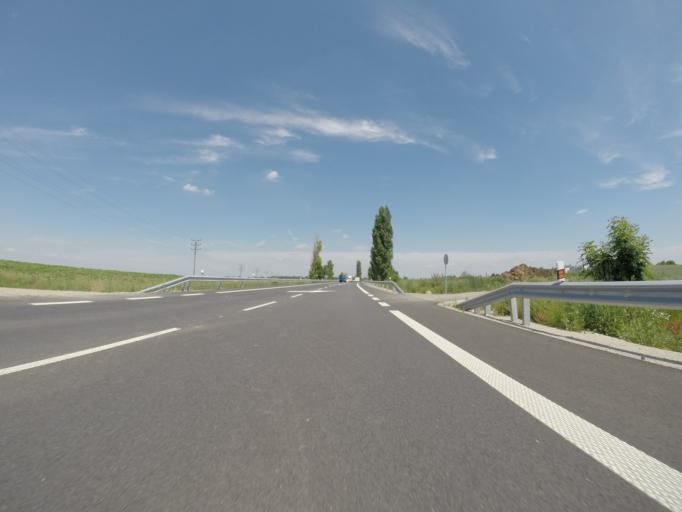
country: SK
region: Trnavsky
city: Sladkovicovo
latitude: 48.2022
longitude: 17.6185
